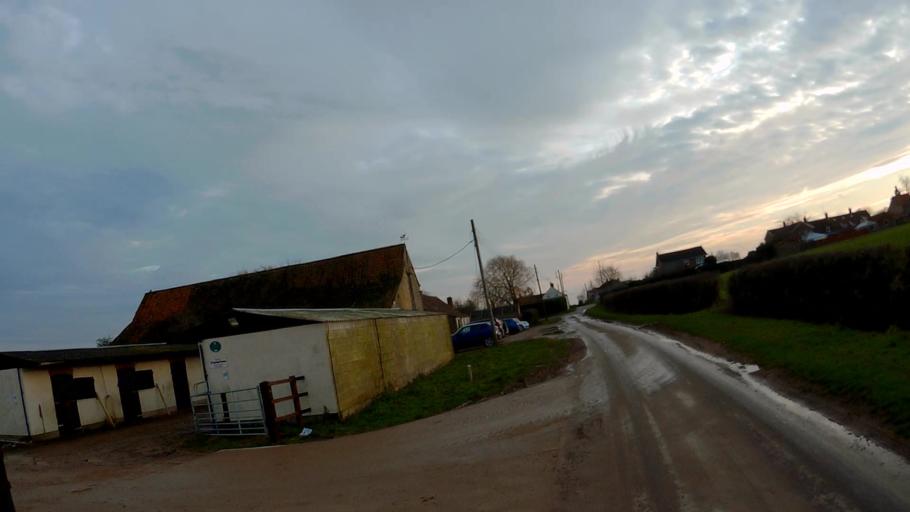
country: GB
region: England
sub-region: Lincolnshire
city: Bourne
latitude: 52.8138
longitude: -0.3989
